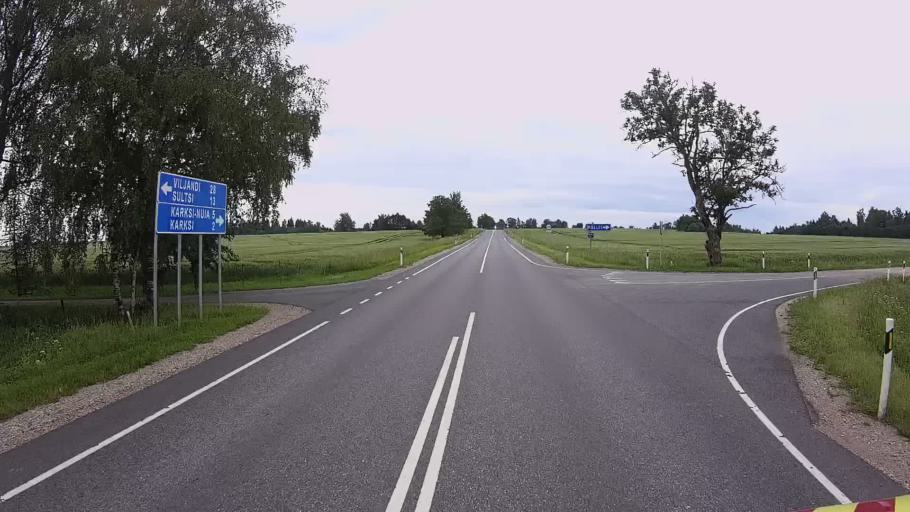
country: EE
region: Viljandimaa
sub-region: Karksi vald
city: Karksi-Nuia
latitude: 58.1396
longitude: 25.5861
